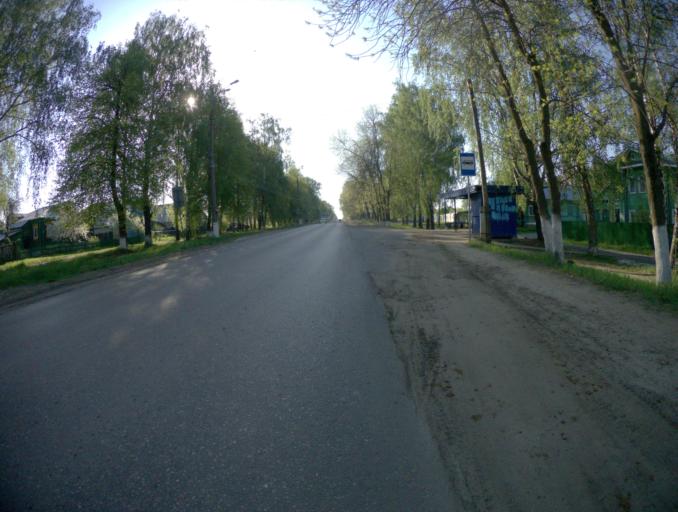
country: RU
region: Vladimir
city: Vyazniki
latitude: 56.2384
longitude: 42.1741
